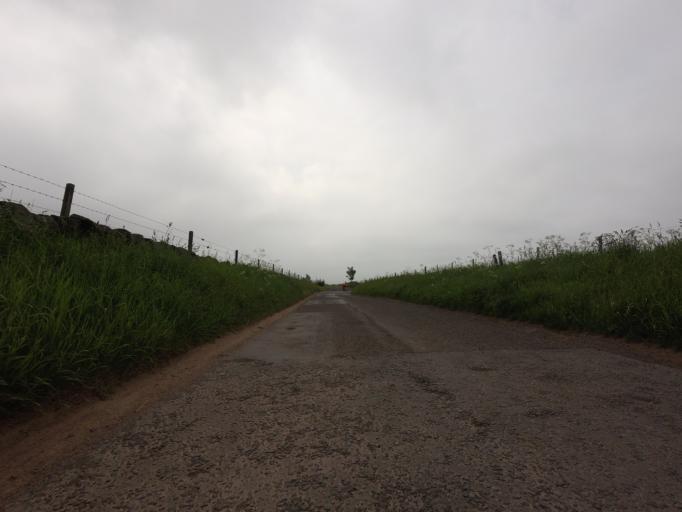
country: GB
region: Scotland
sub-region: Fife
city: Ballingry
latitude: 56.2266
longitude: -3.3412
